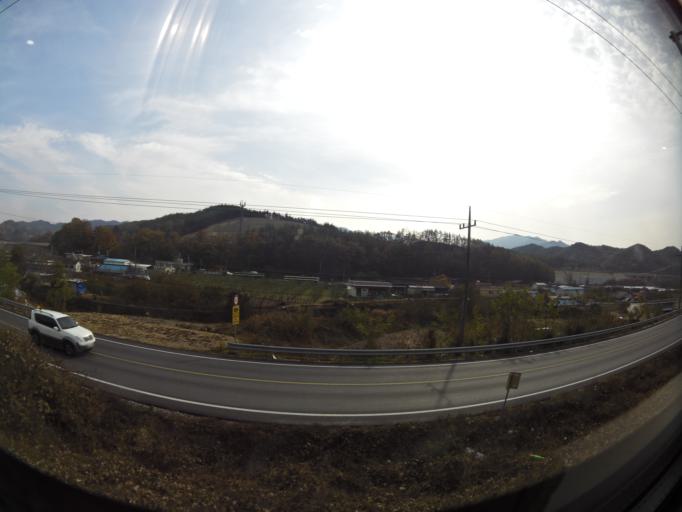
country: KR
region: Chungcheongbuk-do
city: Yong-dong
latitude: 36.1866
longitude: 127.8494
